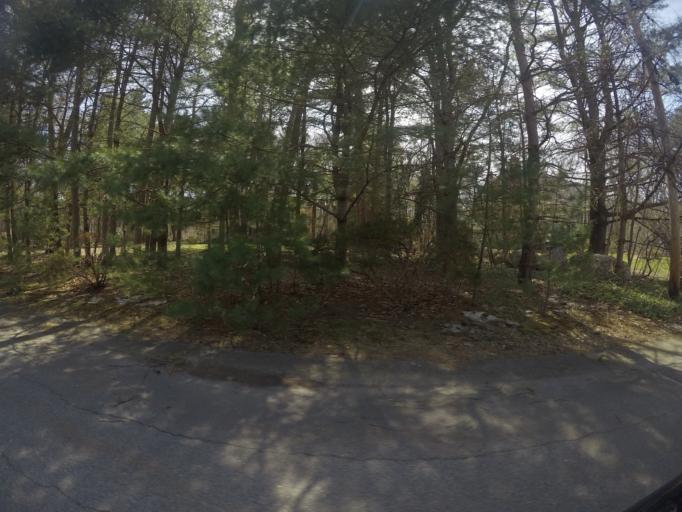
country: US
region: Massachusetts
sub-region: Bristol County
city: Easton
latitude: 42.0226
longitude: -71.0909
